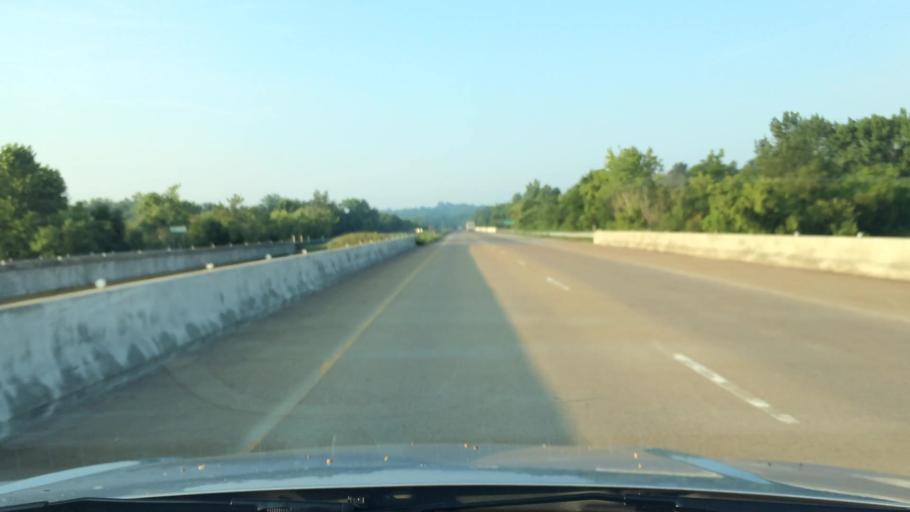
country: US
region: Tennessee
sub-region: Giles County
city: Pulaski
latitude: 35.1985
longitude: -87.0637
